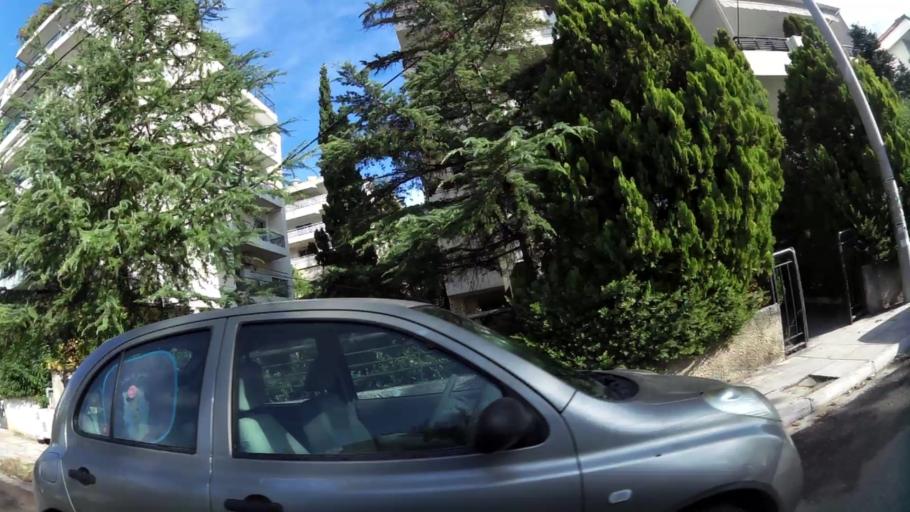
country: GR
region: Attica
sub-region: Nomarchia Athinas
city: Melissia
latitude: 38.0493
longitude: 23.8228
